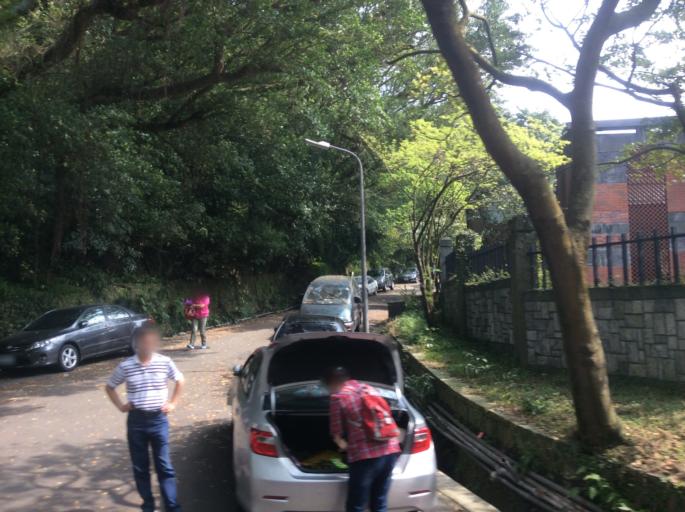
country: TW
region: Taipei
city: Taipei
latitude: 25.1524
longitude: 121.5486
